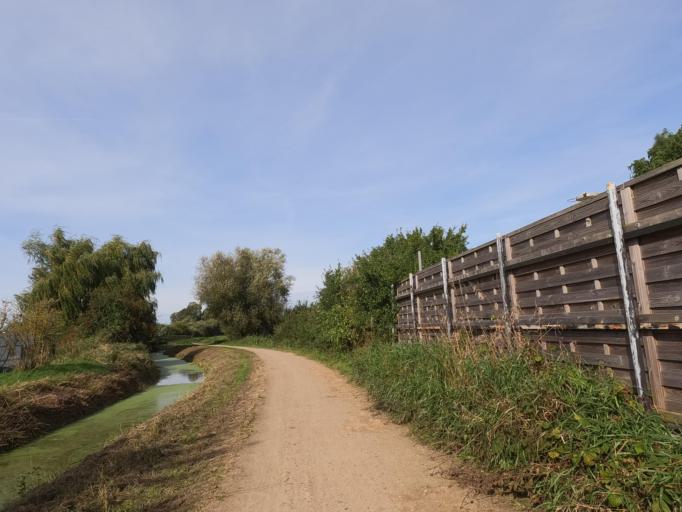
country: DE
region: Schleswig-Holstein
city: Gromitz
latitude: 54.1630
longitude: 10.9950
